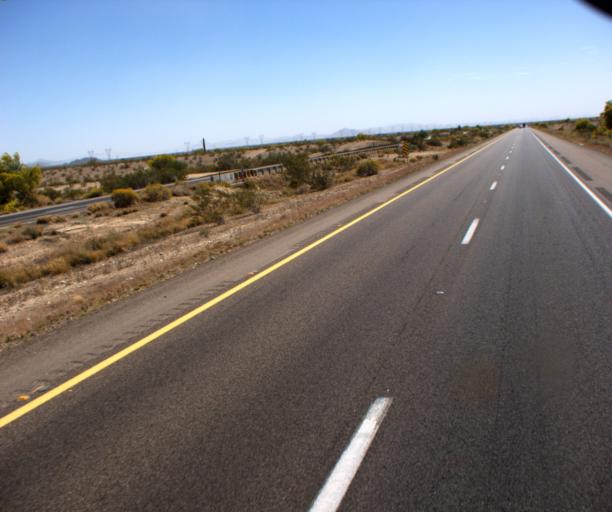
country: US
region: Arizona
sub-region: Maricopa County
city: Gila Bend
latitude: 33.0814
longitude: -112.6474
